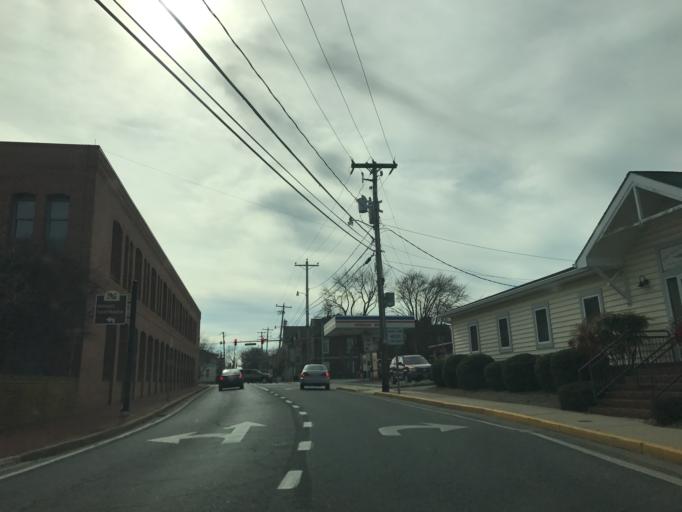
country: US
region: Maryland
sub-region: Queen Anne's County
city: Centreville
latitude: 39.0463
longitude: -76.0653
